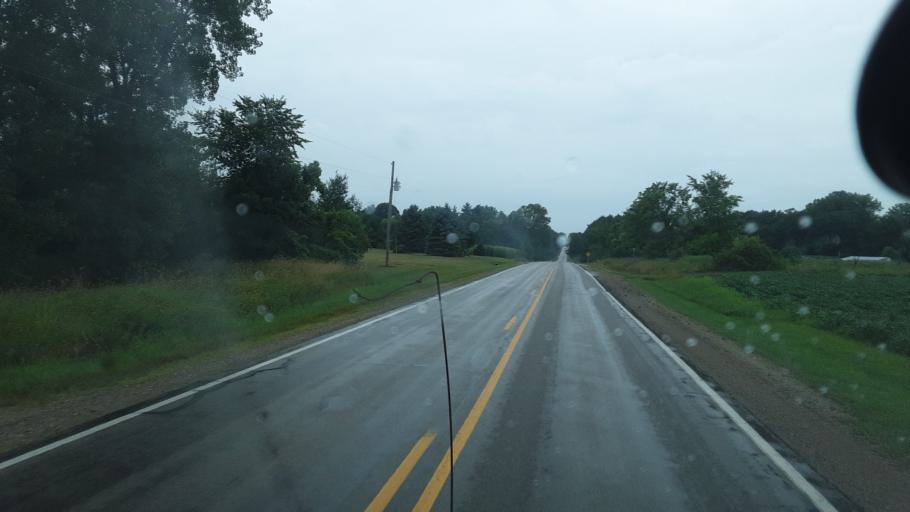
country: US
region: Indiana
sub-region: Steuben County
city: Hamilton
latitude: 41.5590
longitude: -84.8305
